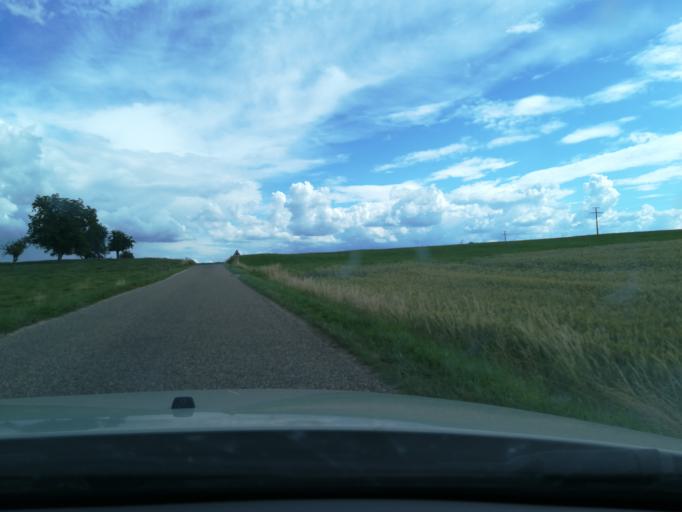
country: FR
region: Alsace
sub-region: Departement du Bas-Rhin
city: Ingwiller
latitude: 48.8612
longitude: 7.4835
